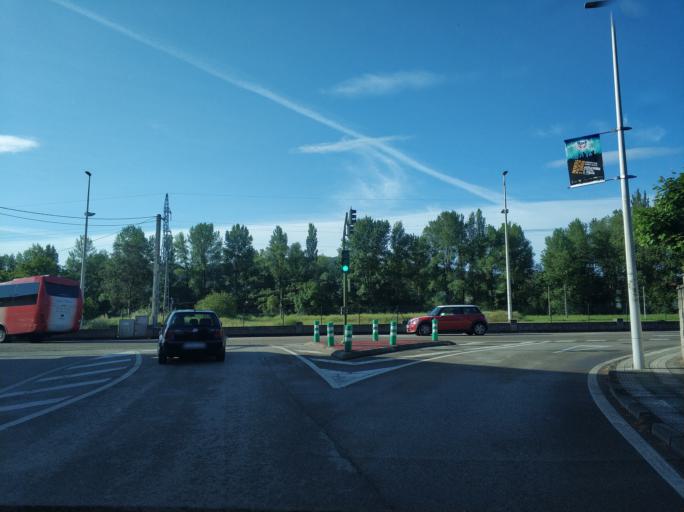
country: ES
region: Cantabria
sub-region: Provincia de Cantabria
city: Polanco
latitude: 43.3569
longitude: -3.9662
